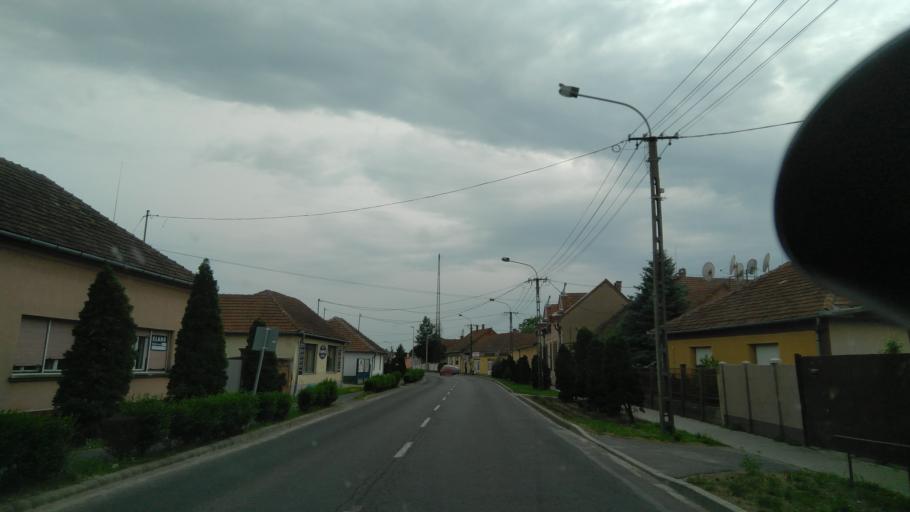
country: HU
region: Bekes
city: Sarkad
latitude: 46.7434
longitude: 21.3819
